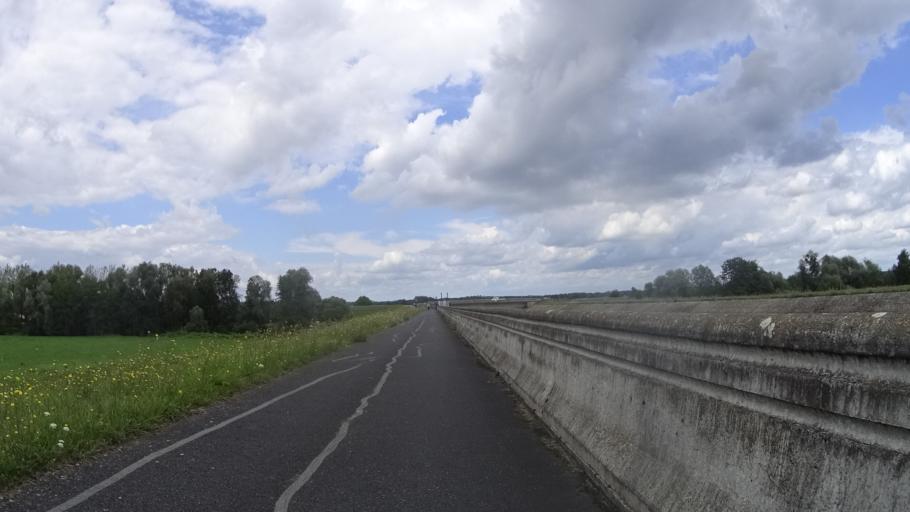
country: FR
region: Champagne-Ardenne
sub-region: Departement de la Haute-Marne
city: Villiers-en-Lieu
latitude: 48.5906
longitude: 4.8574
